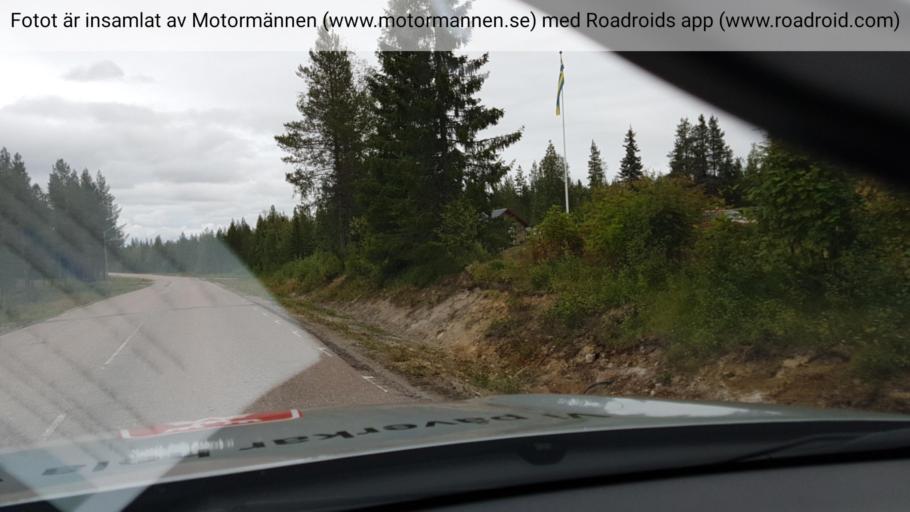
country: SE
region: Norrbotten
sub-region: Overkalix Kommun
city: OEverkalix
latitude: 67.0597
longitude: 22.2250
